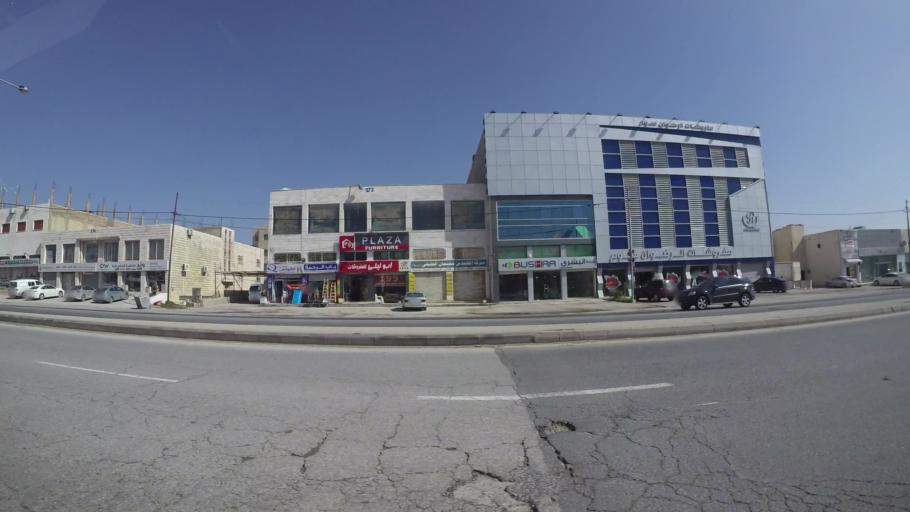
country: JO
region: Amman
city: Al Bunayyat ash Shamaliyah
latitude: 31.8987
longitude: 35.8977
